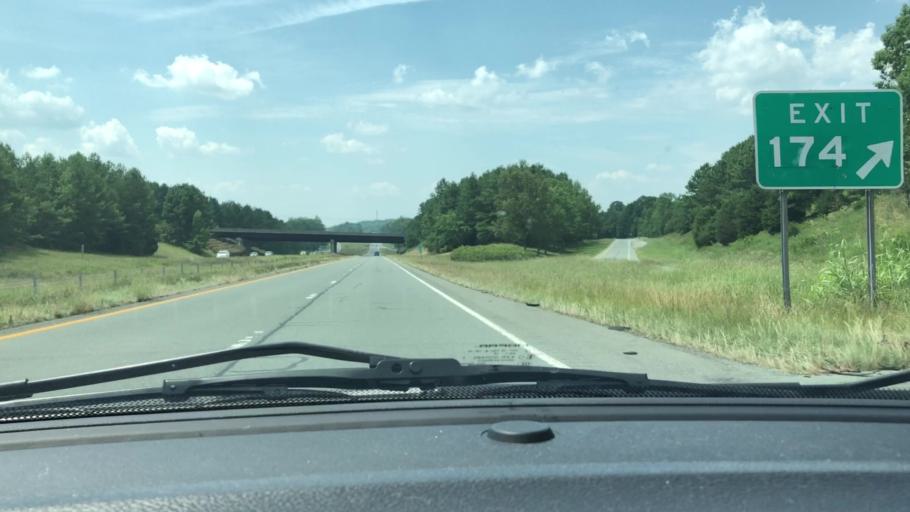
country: US
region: North Carolina
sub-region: Chatham County
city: Siler City
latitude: 35.7624
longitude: -79.4711
